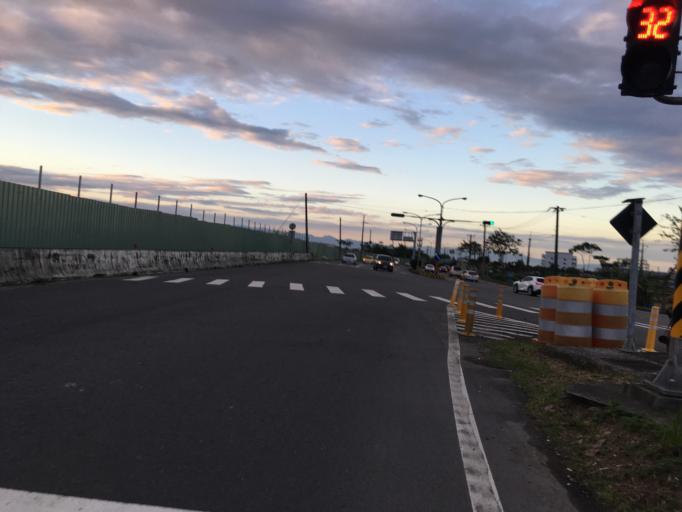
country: TW
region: Taiwan
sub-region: Yilan
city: Yilan
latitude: 24.6276
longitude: 121.8324
